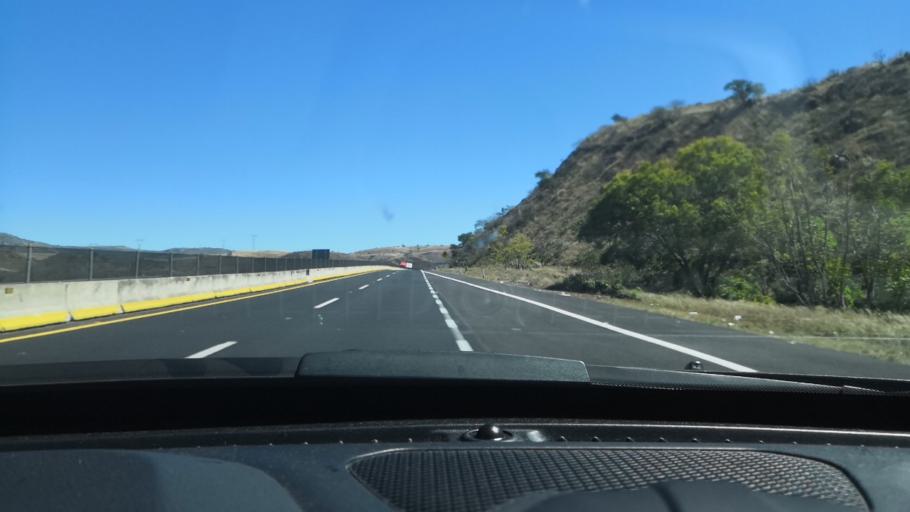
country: MX
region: Nayarit
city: Jala
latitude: 21.0788
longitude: -104.4246
